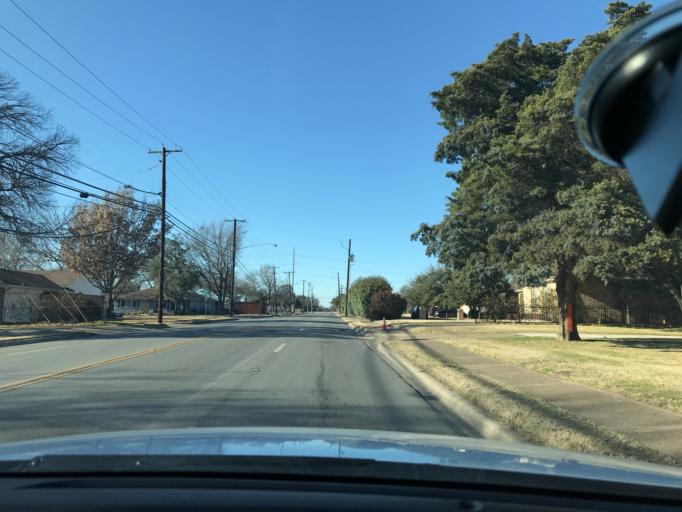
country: US
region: Texas
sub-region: Dallas County
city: Garland
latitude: 32.8308
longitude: -96.6877
